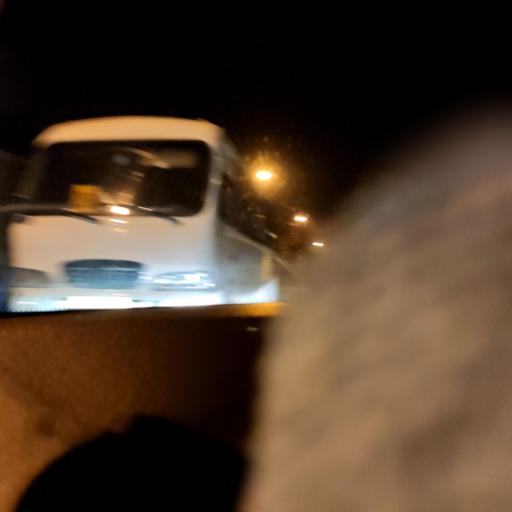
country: RU
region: Samara
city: Smyshlyayevka
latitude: 53.2476
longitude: 50.3428
